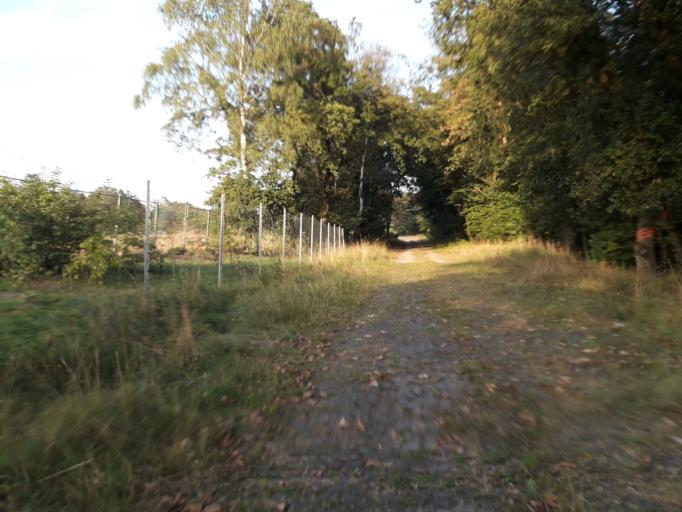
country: DE
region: North Rhine-Westphalia
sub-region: Regierungsbezirk Detmold
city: Augustdorf
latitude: 51.8883
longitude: 8.7373
